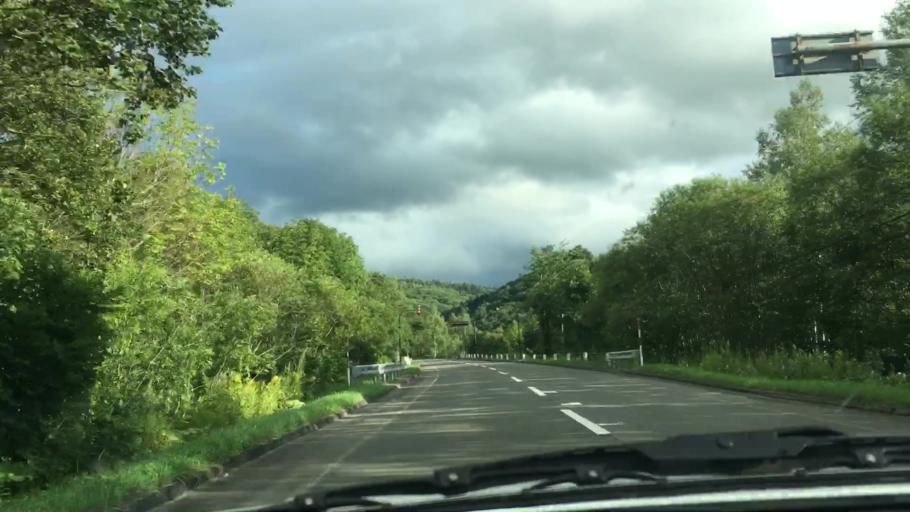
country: JP
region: Hokkaido
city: Shimo-furano
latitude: 43.1124
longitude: 142.6891
